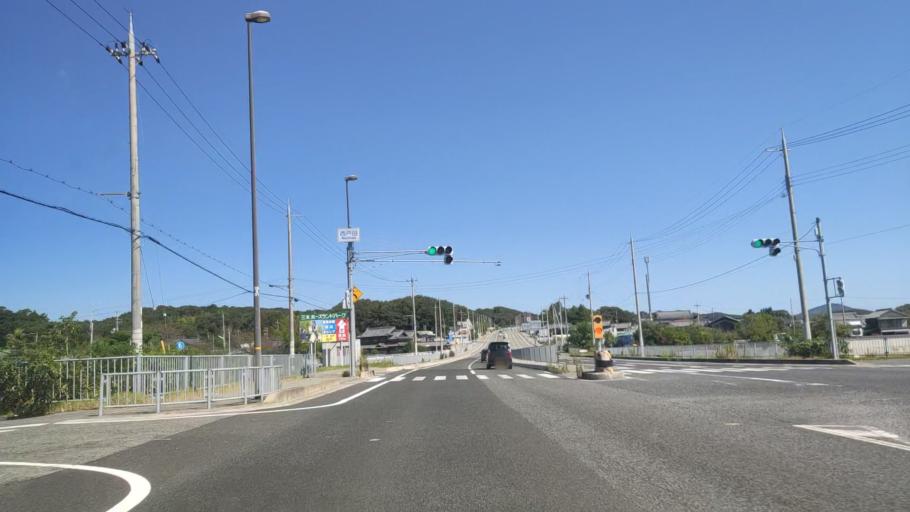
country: JP
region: Hyogo
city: Akashi
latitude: 34.7148
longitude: 134.9835
